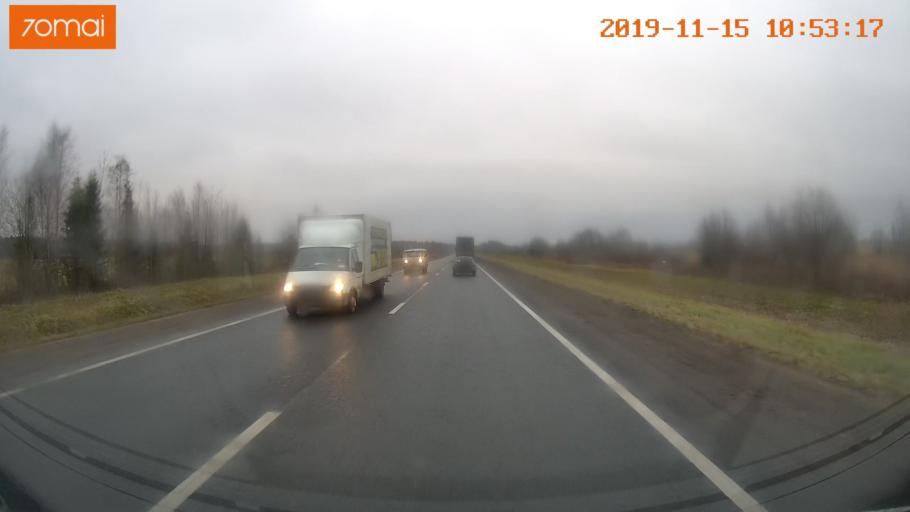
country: RU
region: Vologda
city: Chebsara
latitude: 59.1701
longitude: 38.7505
